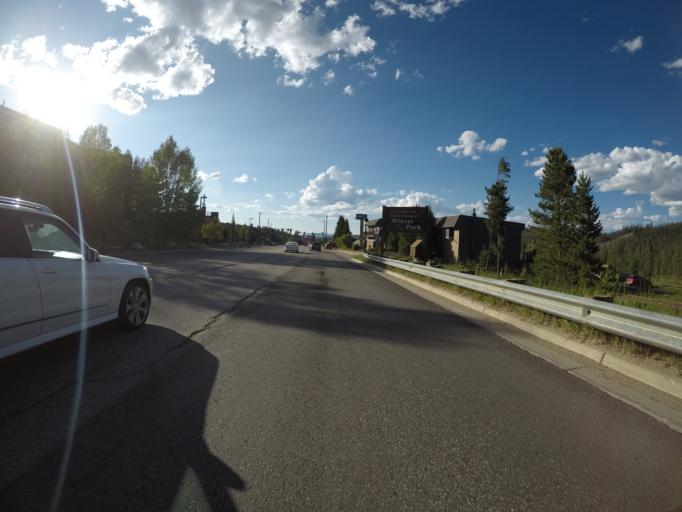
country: US
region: Colorado
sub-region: Grand County
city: Fraser
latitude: 39.9162
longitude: -105.7831
